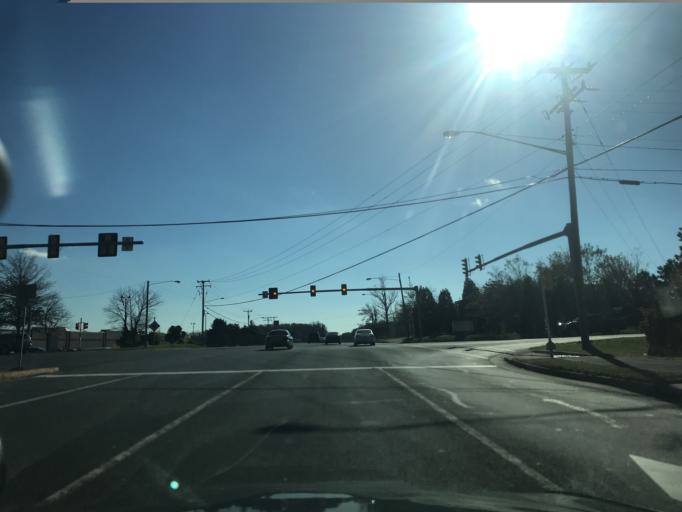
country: US
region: Virginia
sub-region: Fairfax County
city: Greenbriar
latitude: 38.8518
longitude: -77.3728
